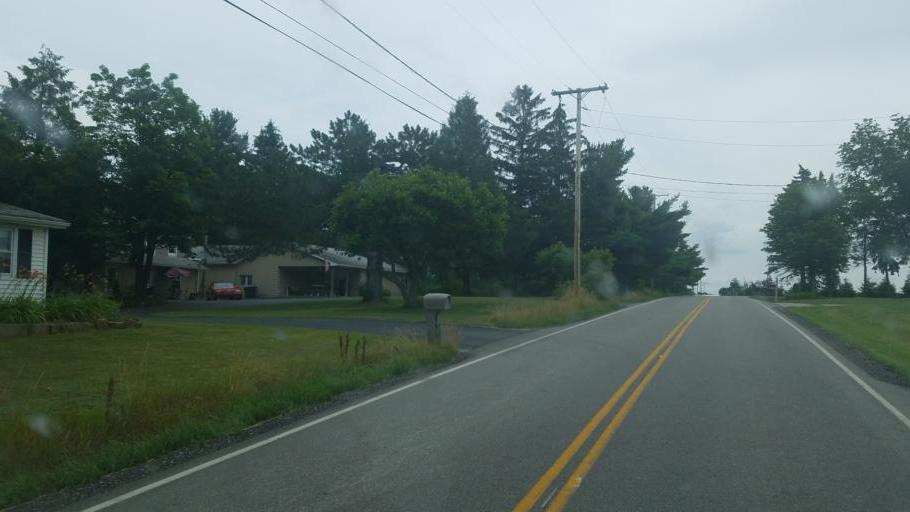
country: US
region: Ohio
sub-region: Geauga County
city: Burton
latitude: 41.4972
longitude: -81.1335
